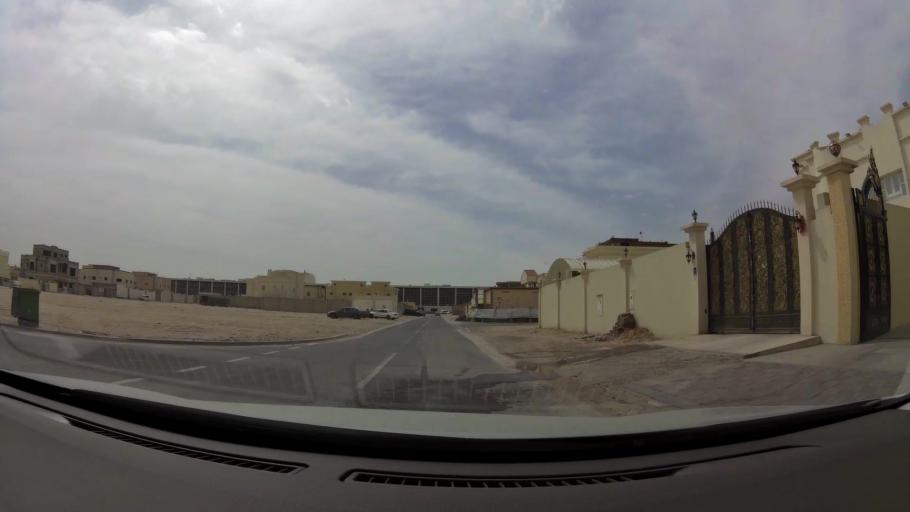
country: QA
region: Al Wakrah
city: Al Wukayr
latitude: 25.1983
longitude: 51.4593
